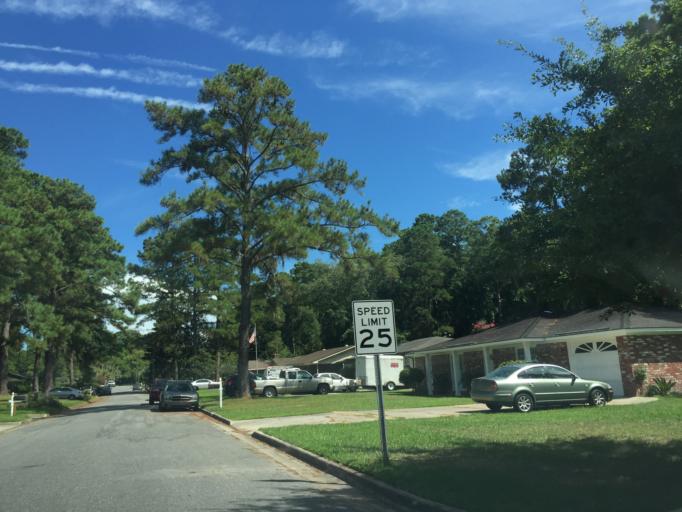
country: US
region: Georgia
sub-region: Chatham County
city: Montgomery
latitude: 31.9795
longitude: -81.1123
